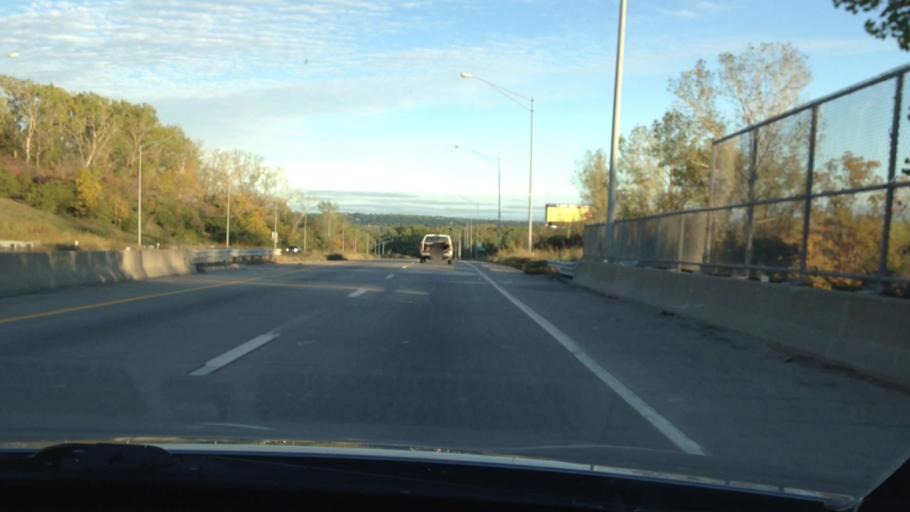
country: US
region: Missouri
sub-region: Clay County
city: Claycomo
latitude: 39.1584
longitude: -94.4874
